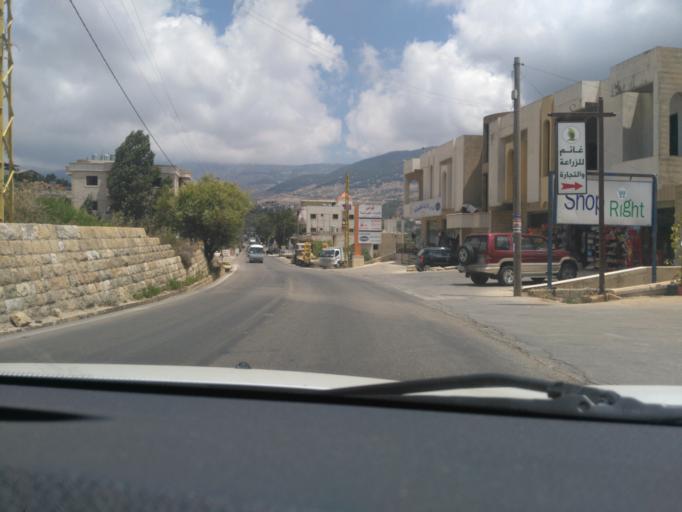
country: LB
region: Mont-Liban
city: Beit ed Dine
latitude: 33.7044
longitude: 35.6646
